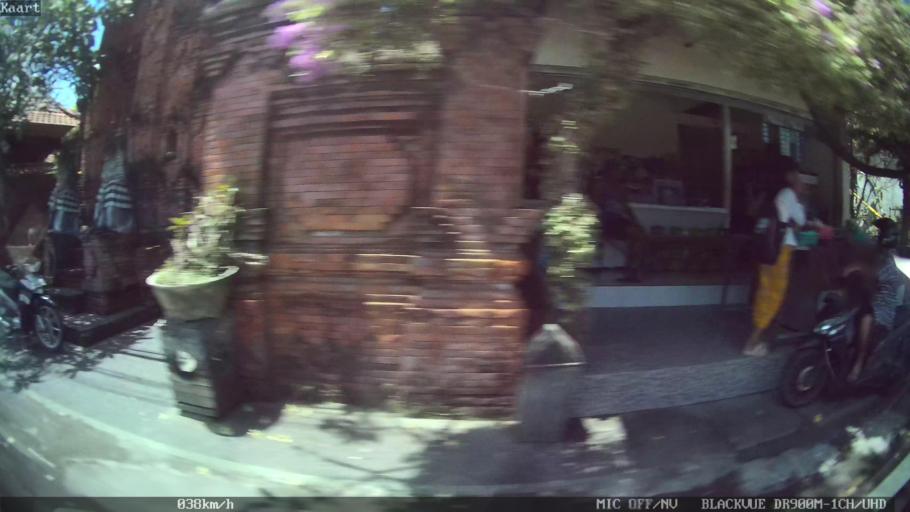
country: ID
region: Bali
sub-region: Kabupaten Gianyar
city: Ubud
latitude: -8.5601
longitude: 115.3171
